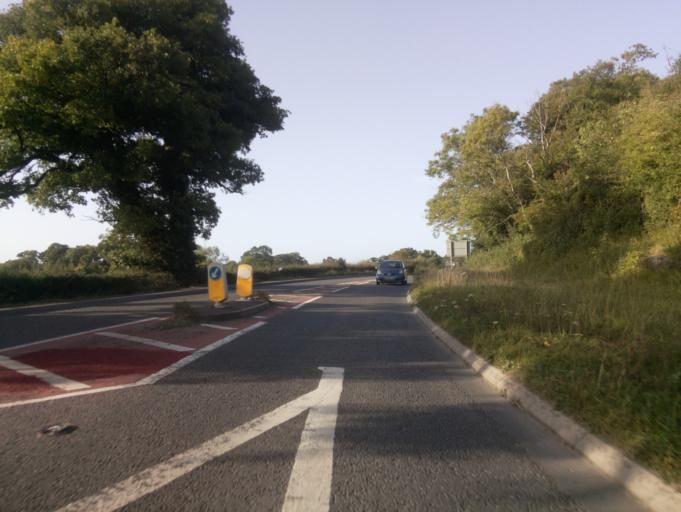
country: GB
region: England
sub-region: Gloucestershire
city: Gloucester
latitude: 51.9084
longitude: -2.2955
